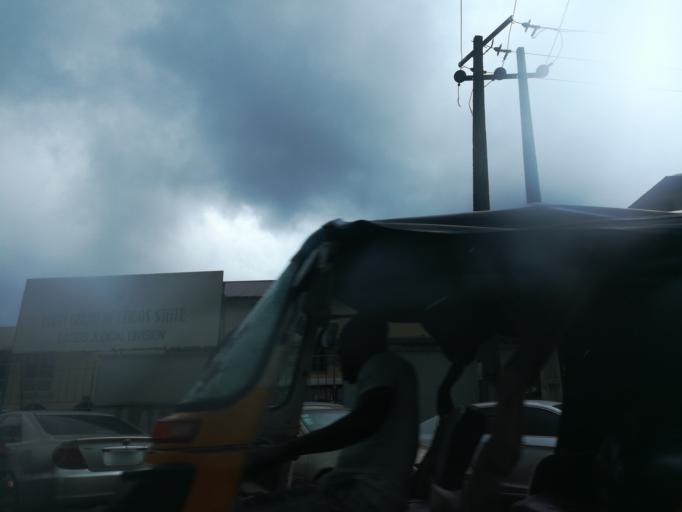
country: NG
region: Lagos
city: Lagos
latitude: 6.4488
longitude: 3.4014
